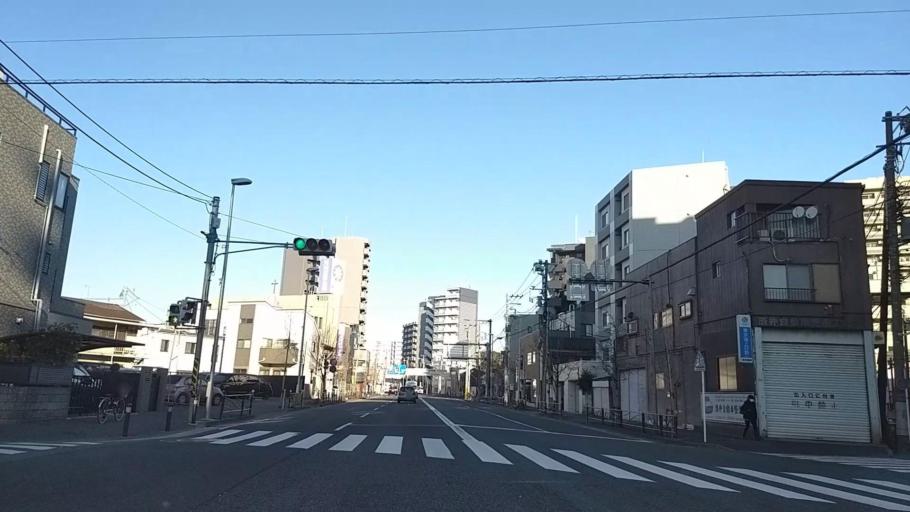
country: JP
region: Kanagawa
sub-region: Kawasaki-shi
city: Kawasaki
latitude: 35.5336
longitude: 139.6893
